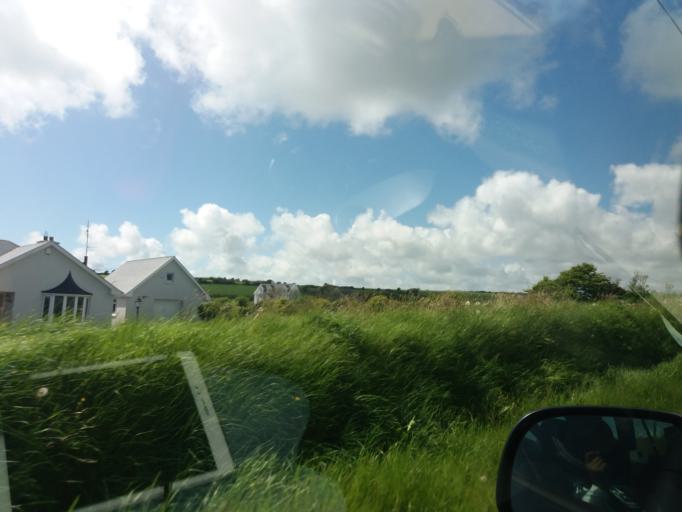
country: IE
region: Munster
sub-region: Waterford
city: Dunmore East
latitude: 52.1893
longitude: -6.8963
